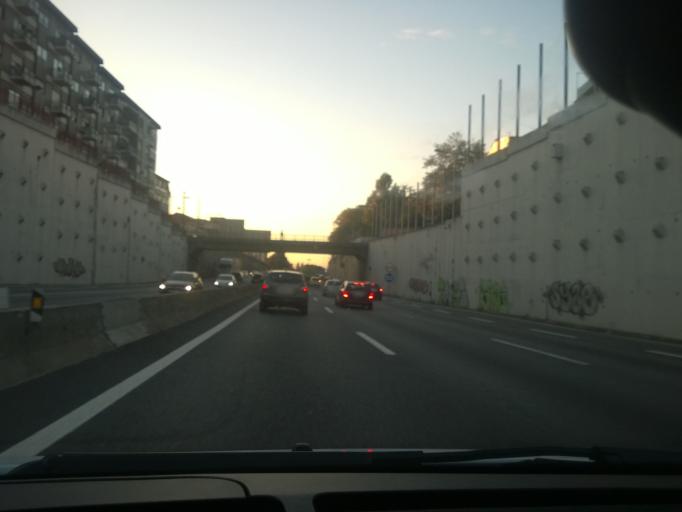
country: PT
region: Porto
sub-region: Maia
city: Pedroucos
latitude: 41.1686
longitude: -8.5897
